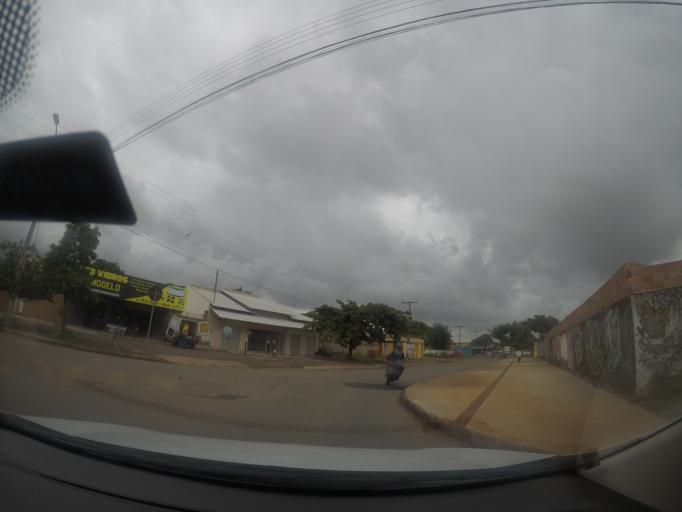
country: BR
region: Goias
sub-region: Trindade
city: Trindade
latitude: -16.6464
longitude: -49.3893
